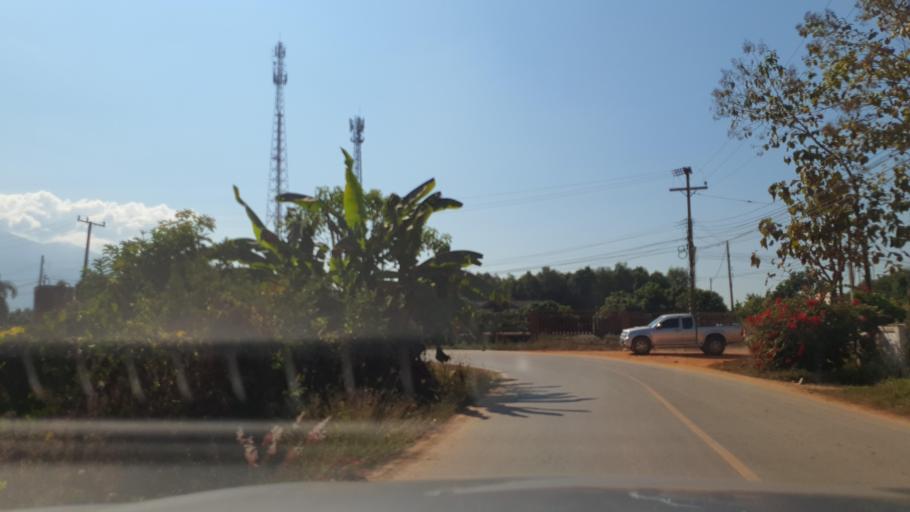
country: TH
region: Nan
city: Pua
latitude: 19.1419
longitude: 100.9241
